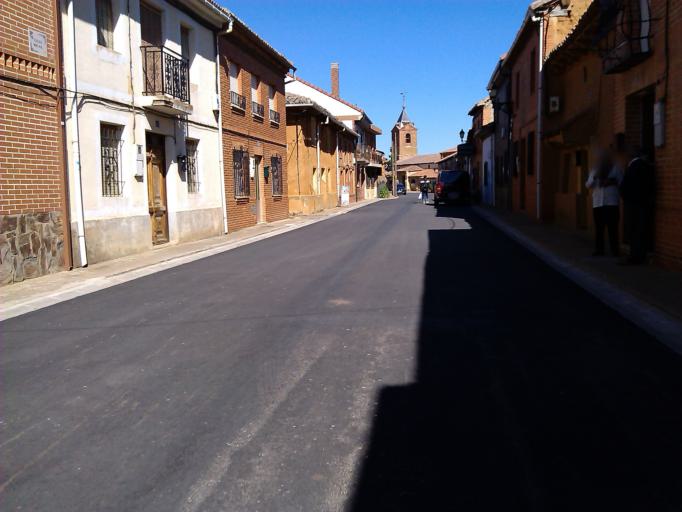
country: ES
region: Castille and Leon
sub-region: Provincia de Leon
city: Vallecillo
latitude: 42.4219
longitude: -5.2188
